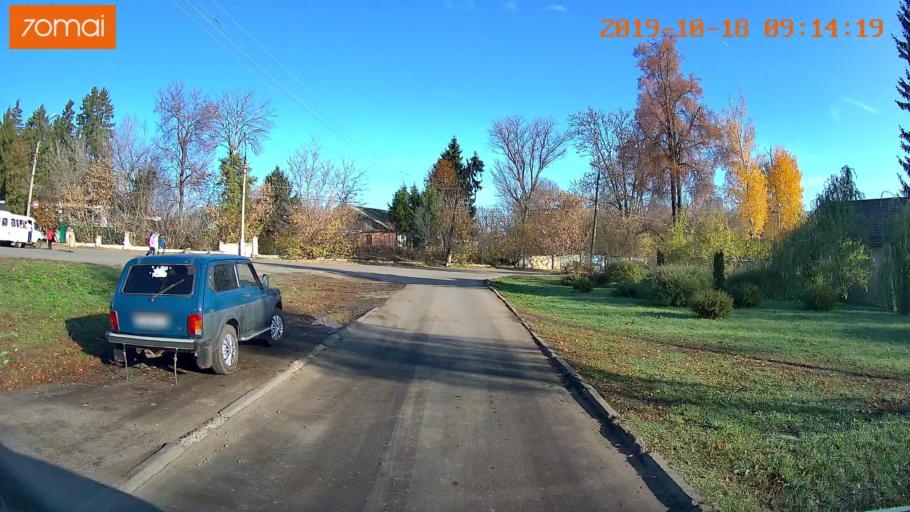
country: RU
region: Tula
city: Yefremov
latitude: 53.1323
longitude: 38.1123
